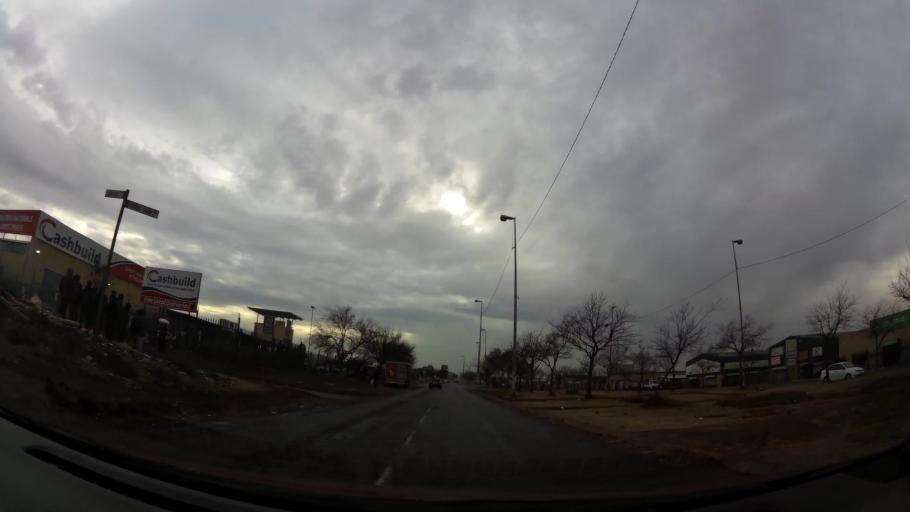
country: ZA
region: Gauteng
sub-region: City of Johannesburg Metropolitan Municipality
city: Soweto
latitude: -26.2882
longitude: 27.8477
